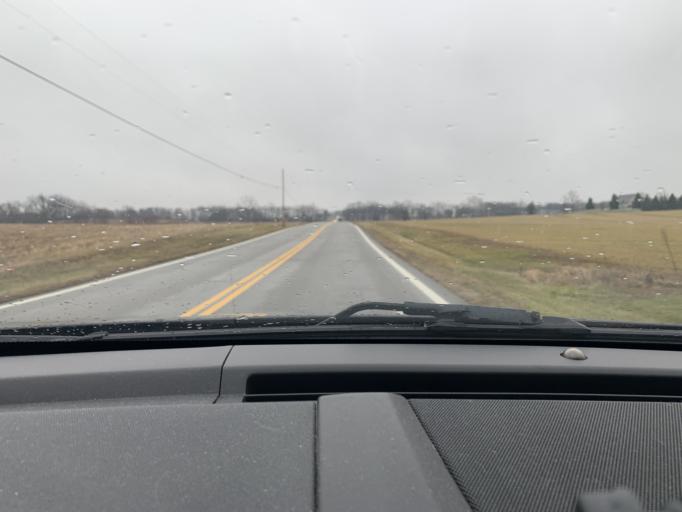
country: US
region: Ohio
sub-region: Ross County
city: Kingston
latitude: 39.4309
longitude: -82.9129
